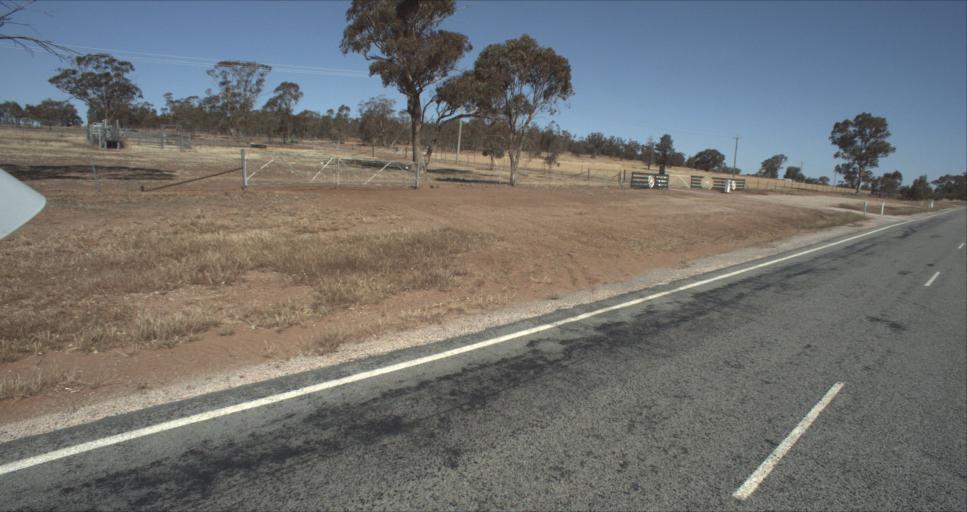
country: AU
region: New South Wales
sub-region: Leeton
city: Leeton
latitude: -34.4742
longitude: 146.4354
